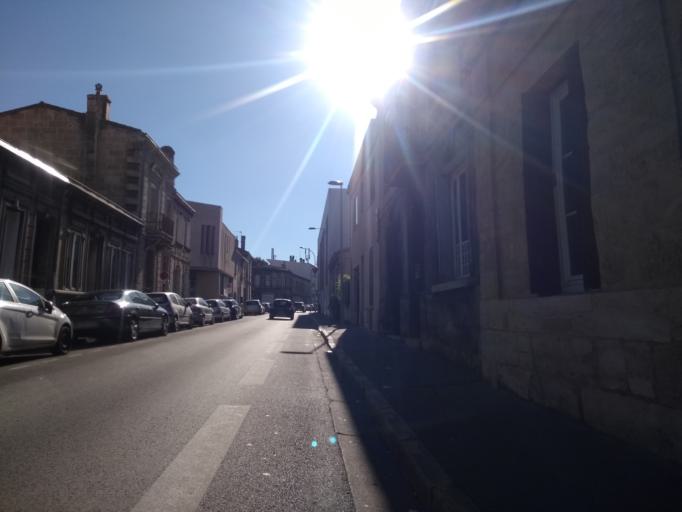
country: FR
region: Aquitaine
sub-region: Departement de la Gironde
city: Begles
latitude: 44.8253
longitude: -0.5630
